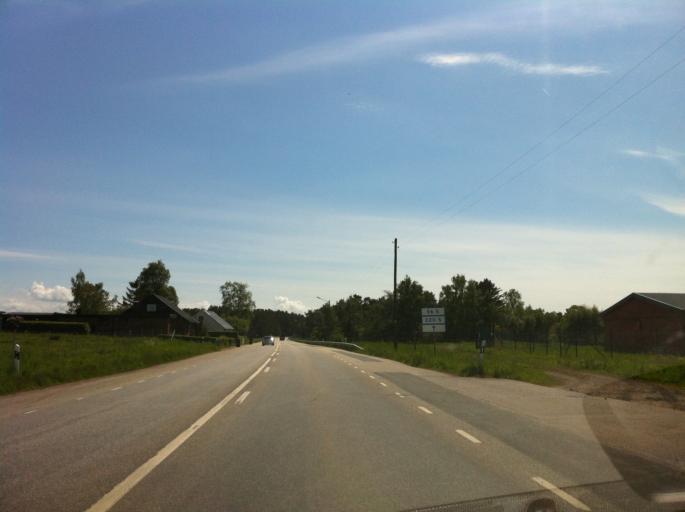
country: SE
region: Skane
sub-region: Landskrona
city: Asmundtorp
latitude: 55.8448
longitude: 12.9657
